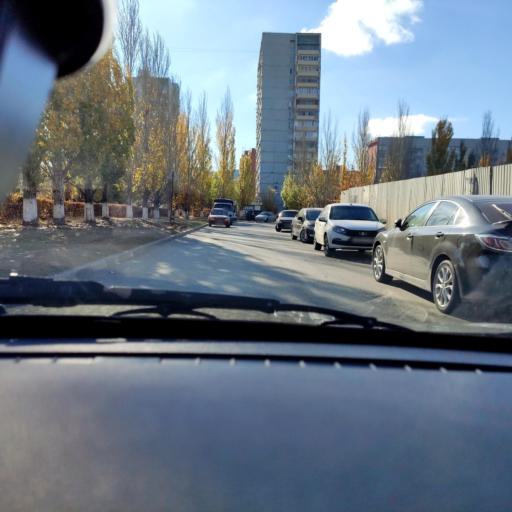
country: RU
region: Samara
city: Tol'yatti
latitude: 53.5377
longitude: 49.3380
